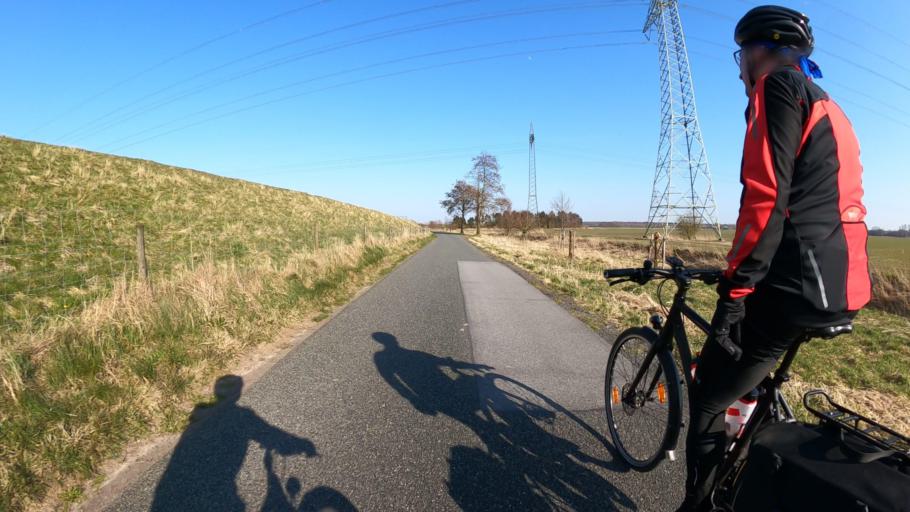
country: DE
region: Schleswig-Holstein
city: Seester
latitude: 53.7347
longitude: 9.6082
